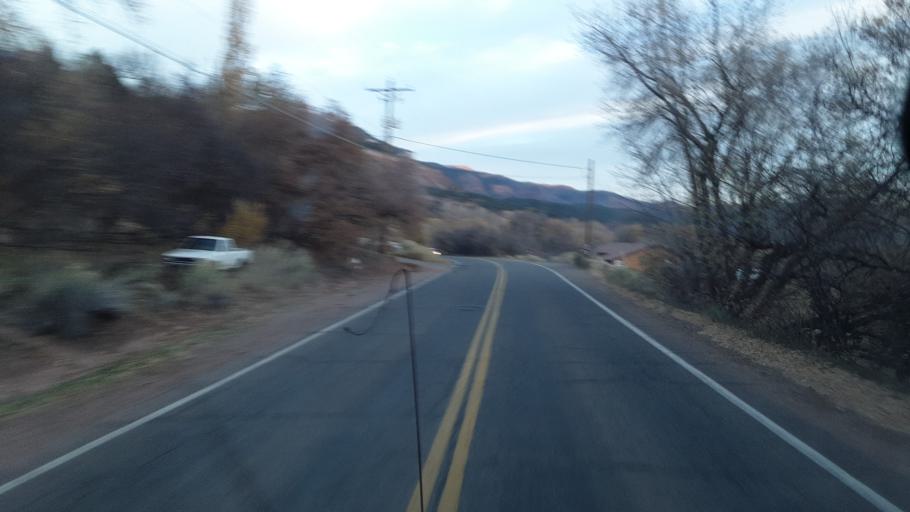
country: US
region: Colorado
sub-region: La Plata County
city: Durango
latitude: 37.3289
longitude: -107.8533
